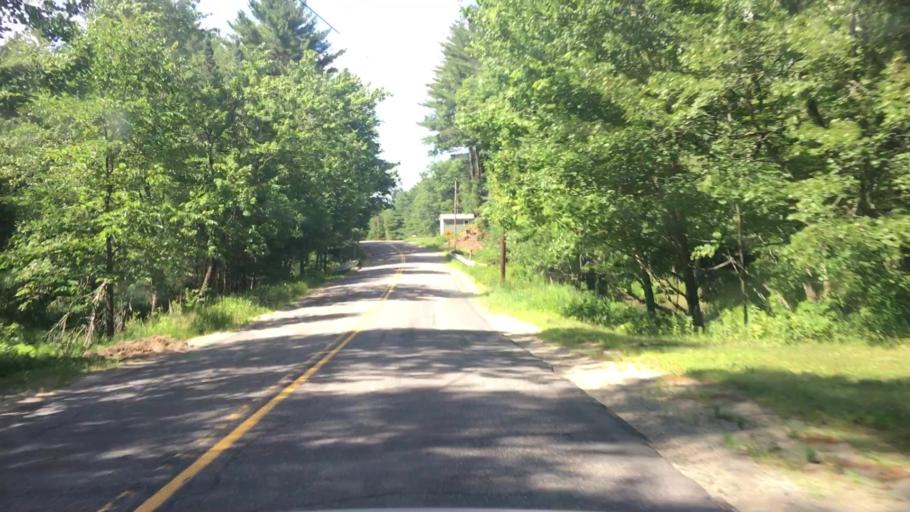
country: US
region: Maine
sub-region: Franklin County
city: Chesterville
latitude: 44.5676
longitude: -70.0869
